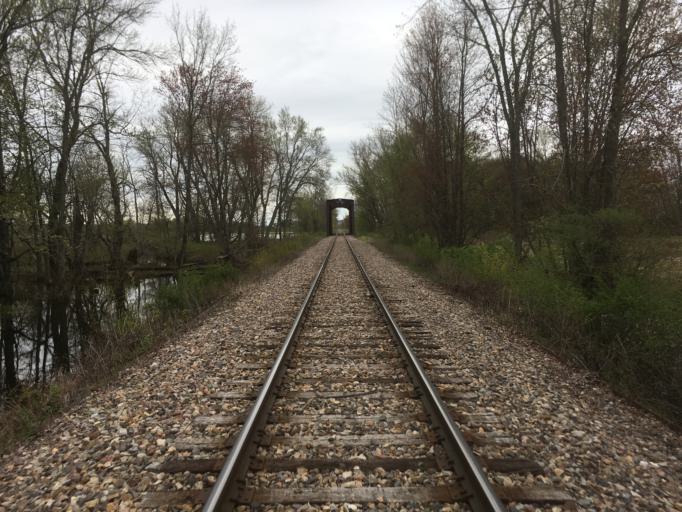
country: US
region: Vermont
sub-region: Addison County
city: Middlebury (village)
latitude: 43.9540
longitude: -73.1621
